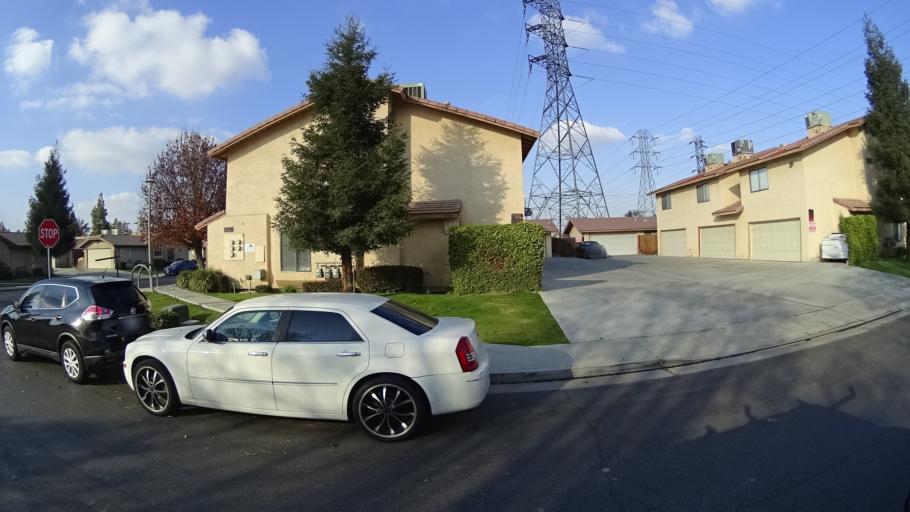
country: US
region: California
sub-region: Kern County
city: Greenacres
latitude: 35.3174
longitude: -119.0943
